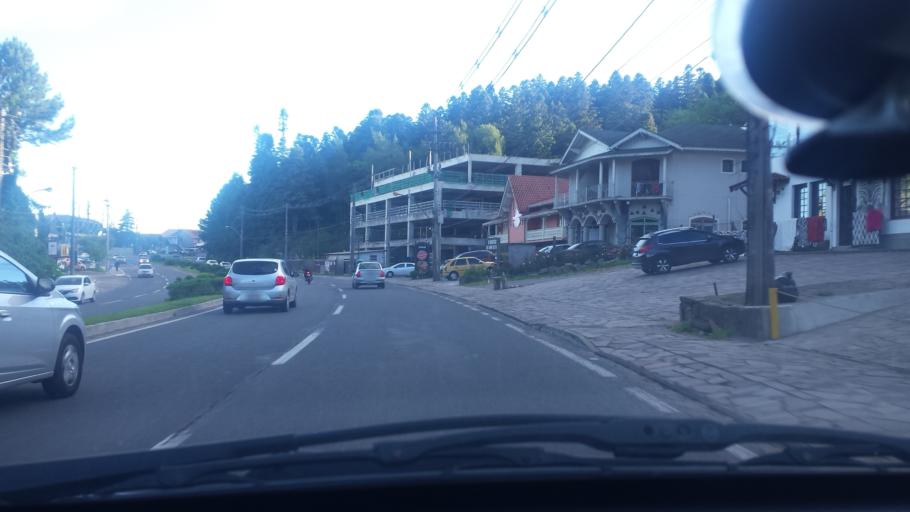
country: BR
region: Rio Grande do Sul
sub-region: Canela
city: Canela
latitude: -29.3741
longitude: -50.8649
